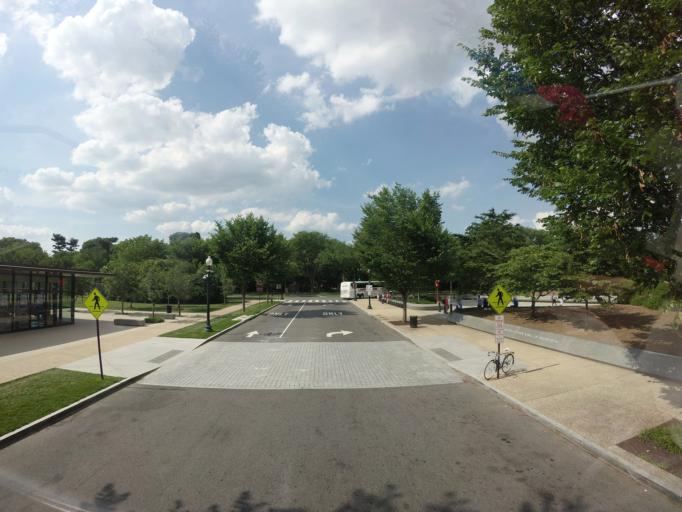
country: US
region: Washington, D.C.
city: Washington, D.C.
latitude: 38.8863
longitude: -77.0449
